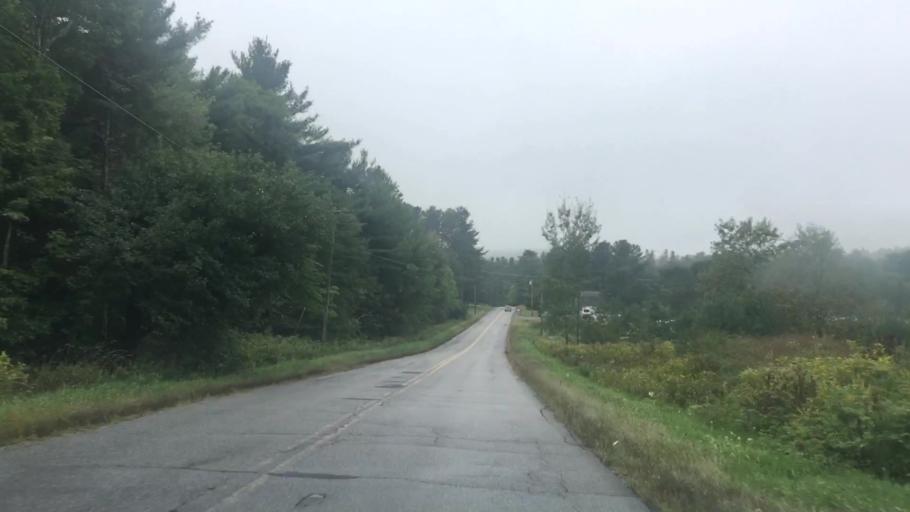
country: US
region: Maine
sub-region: Waldo County
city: Frankfort
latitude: 44.5520
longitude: -68.8673
